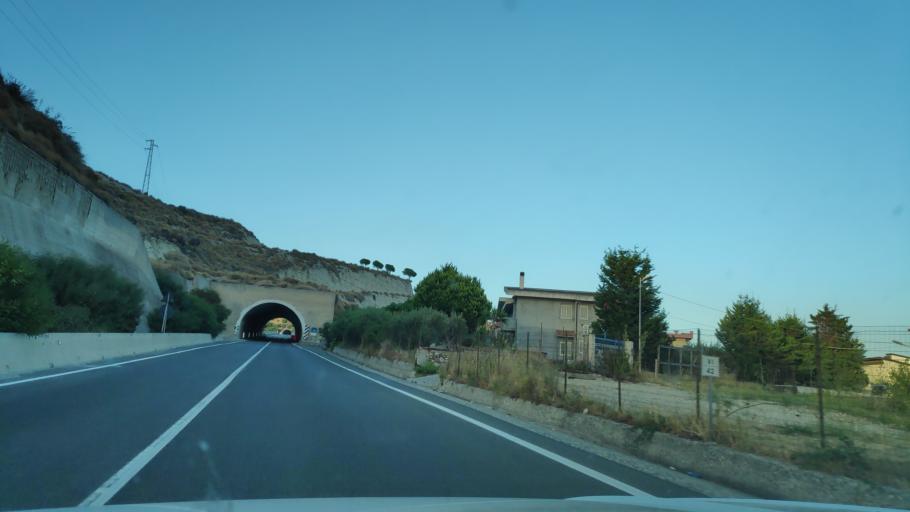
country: IT
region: Calabria
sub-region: Provincia di Reggio Calabria
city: Bova Marina
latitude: 37.9295
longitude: 15.9059
